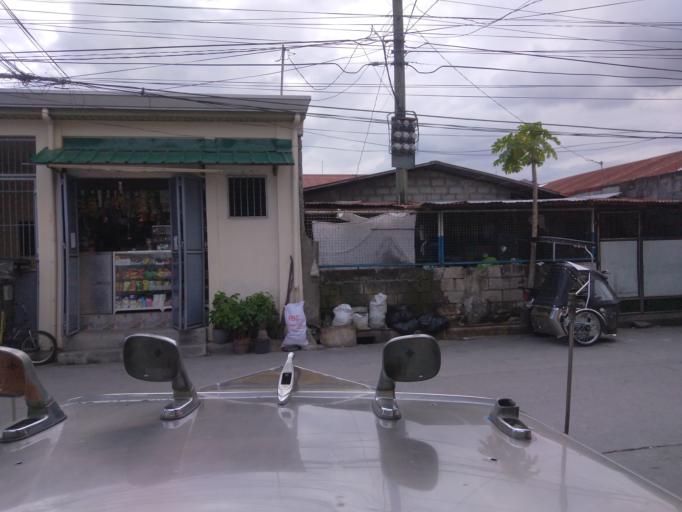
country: PH
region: Central Luzon
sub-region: Province of Pampanga
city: Pandacaqui
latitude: 15.1752
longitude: 120.6459
